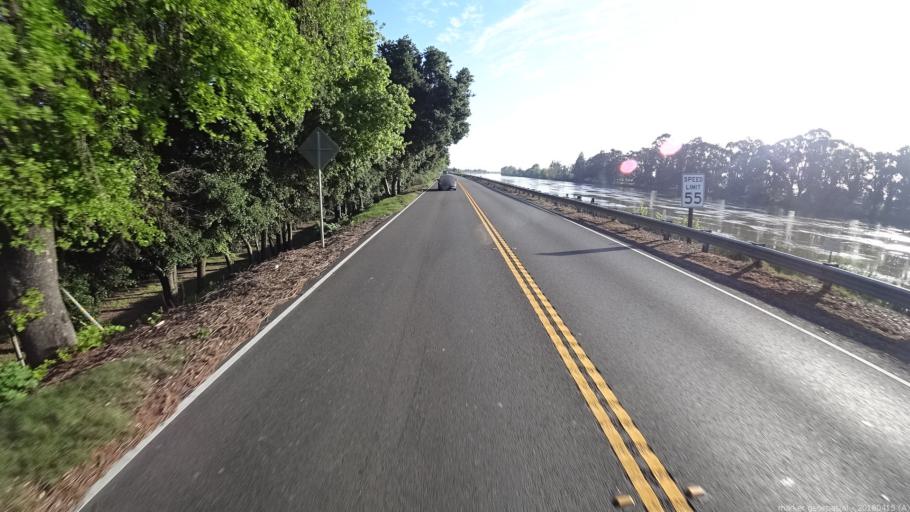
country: US
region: California
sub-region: Solano County
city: Rio Vista
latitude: 38.1739
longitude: -121.5939
